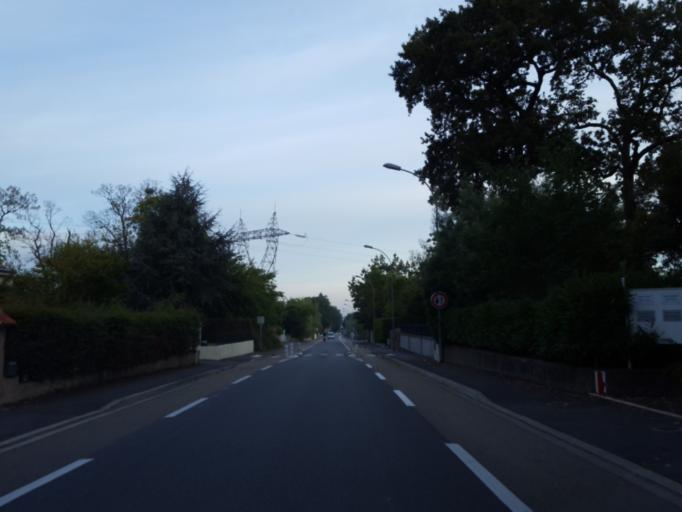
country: FR
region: Pays de la Loire
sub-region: Departement de la Loire-Atlantique
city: Basse-Goulaine
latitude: 47.1963
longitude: -1.4643
